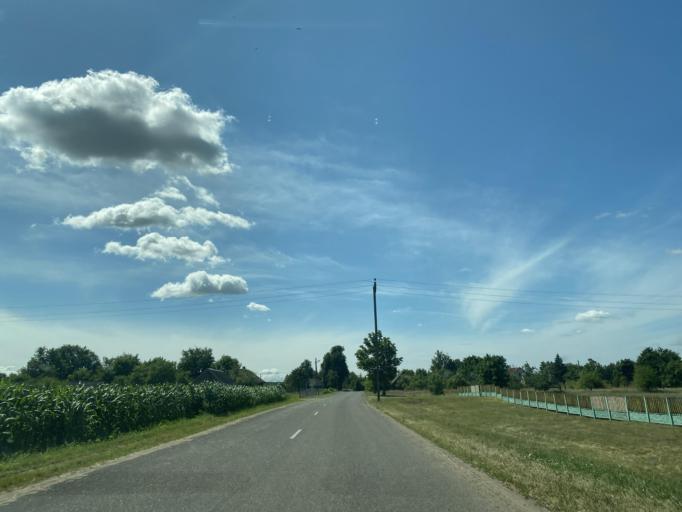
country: BY
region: Brest
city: Ivanava
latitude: 52.2090
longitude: 25.6289
